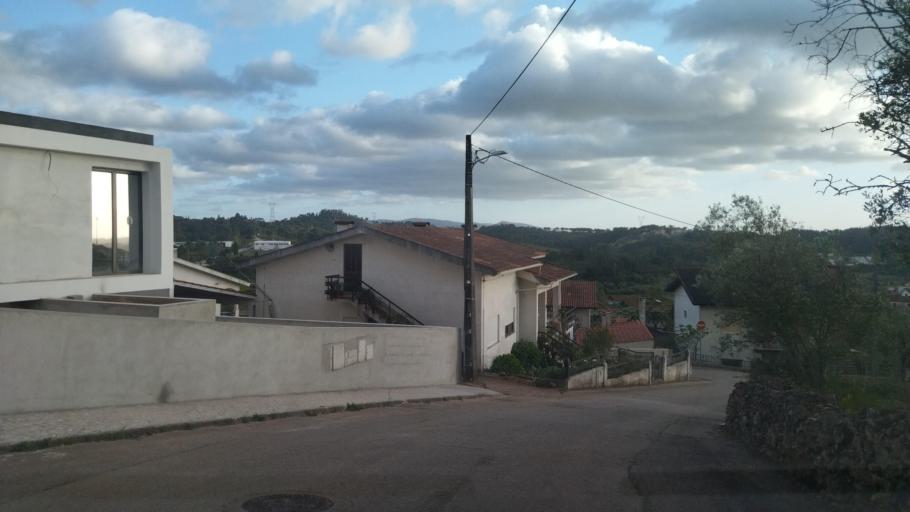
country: PT
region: Coimbra
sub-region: Coimbra
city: Coimbra
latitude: 40.1654
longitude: -8.4477
